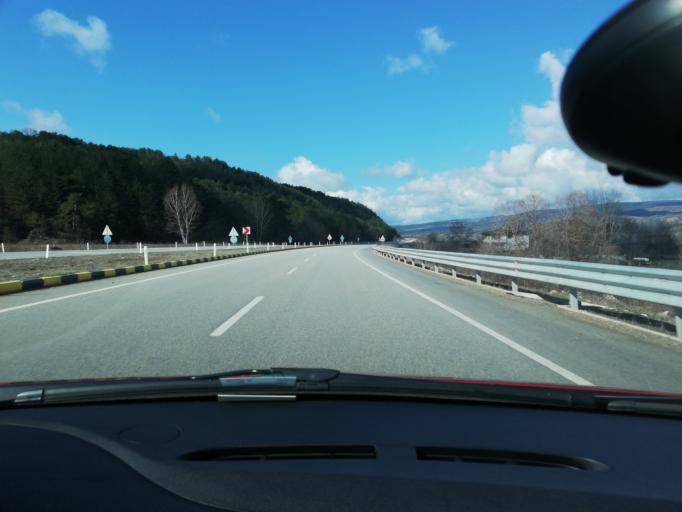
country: TR
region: Kastamonu
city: Arac
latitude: 41.2279
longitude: 33.2796
